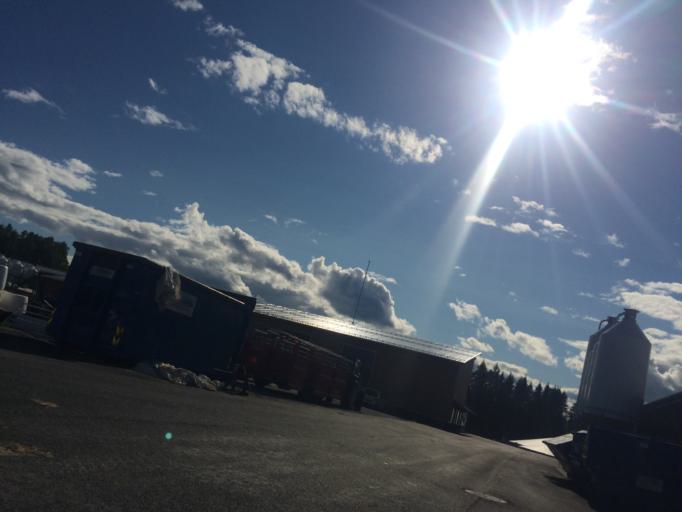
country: NO
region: Akershus
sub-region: As
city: As
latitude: 59.6772
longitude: 10.7651
